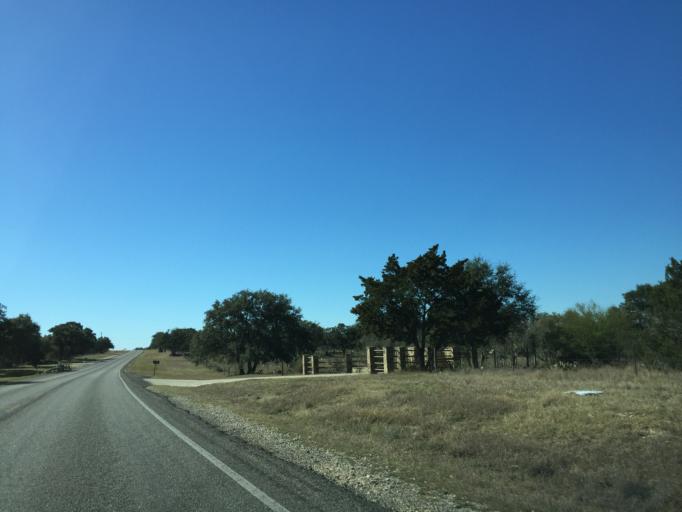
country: US
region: Texas
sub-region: Comal County
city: Garden Ridge
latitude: 29.7399
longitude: -98.3043
